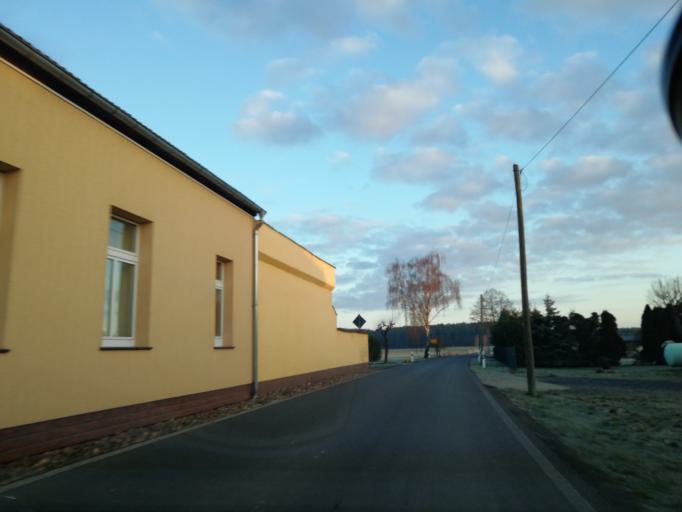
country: DE
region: Brandenburg
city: Crinitz
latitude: 51.7346
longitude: 13.8306
